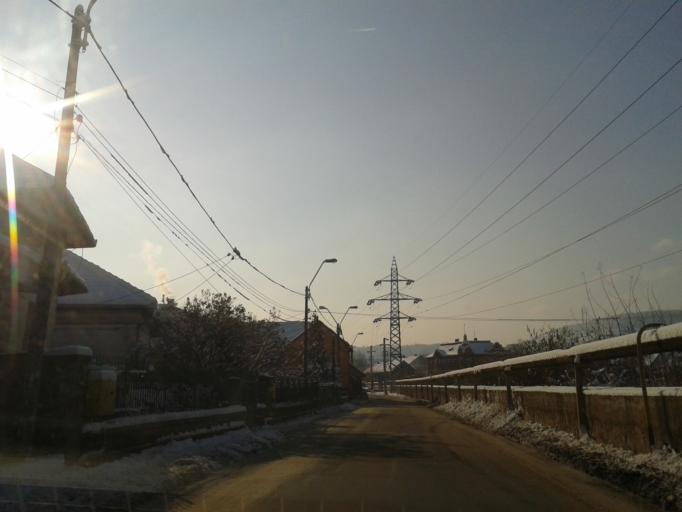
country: RO
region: Hunedoara
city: Hunedoara
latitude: 45.7539
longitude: 22.8951
